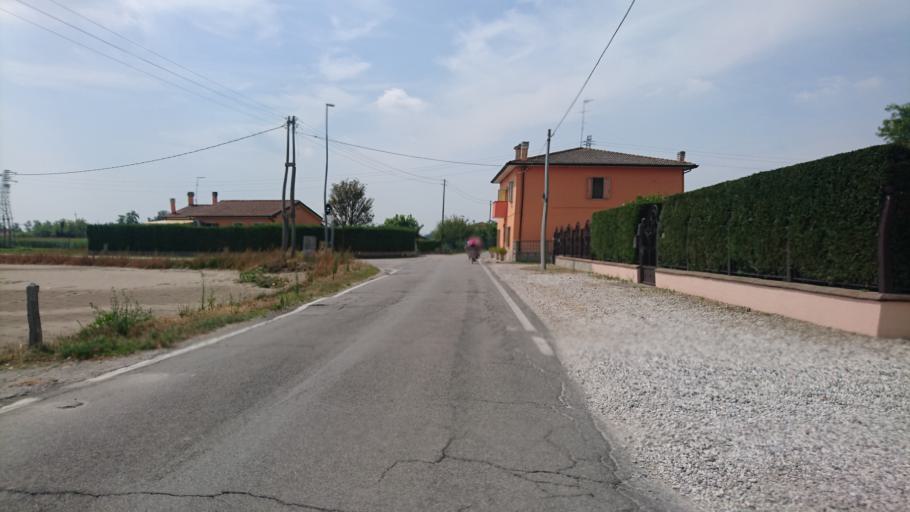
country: IT
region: Veneto
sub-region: Provincia di Rovigo
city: Rosolina
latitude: 45.0870
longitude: 12.2355
